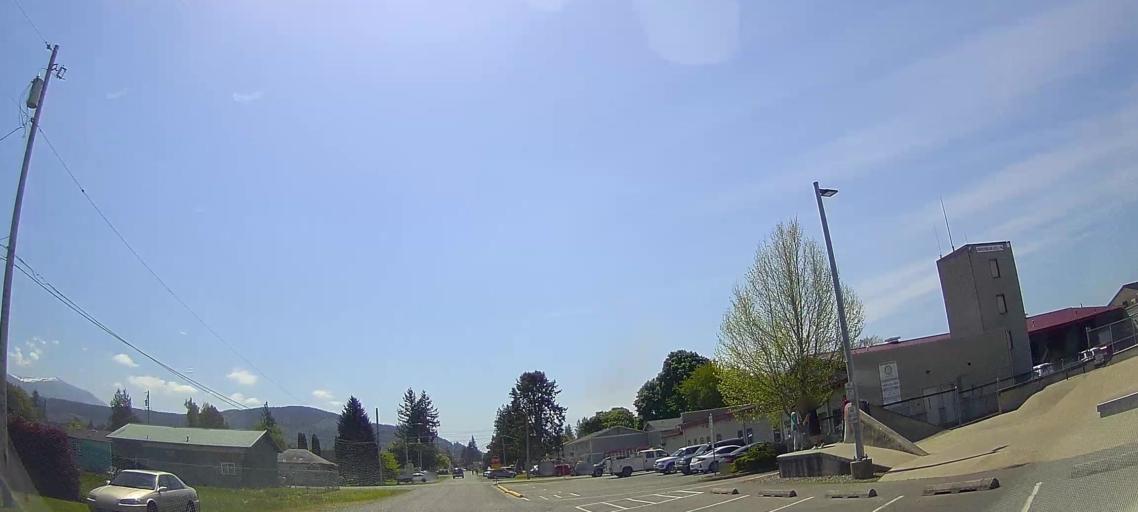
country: US
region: Washington
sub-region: Skagit County
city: Sedro-Woolley
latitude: 48.5092
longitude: -122.2368
